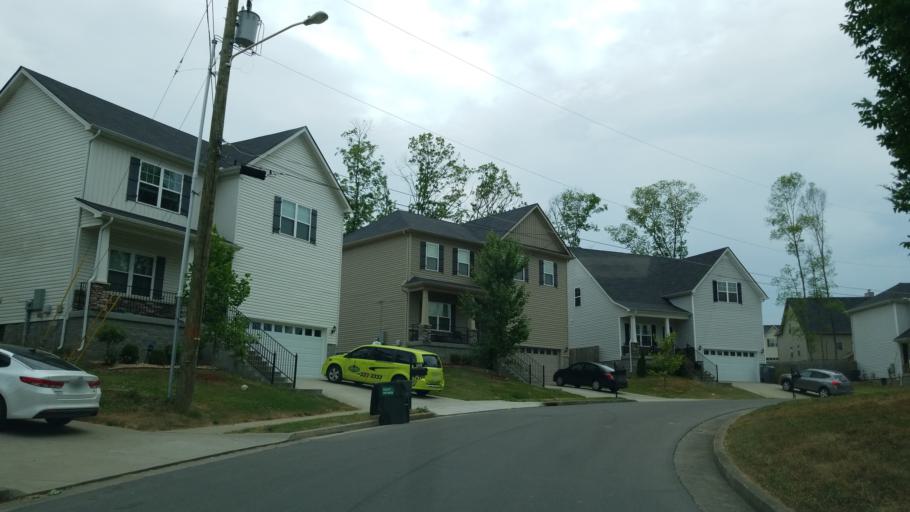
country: US
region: Tennessee
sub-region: Rutherford County
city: La Vergne
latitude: 36.0540
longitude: -86.6040
